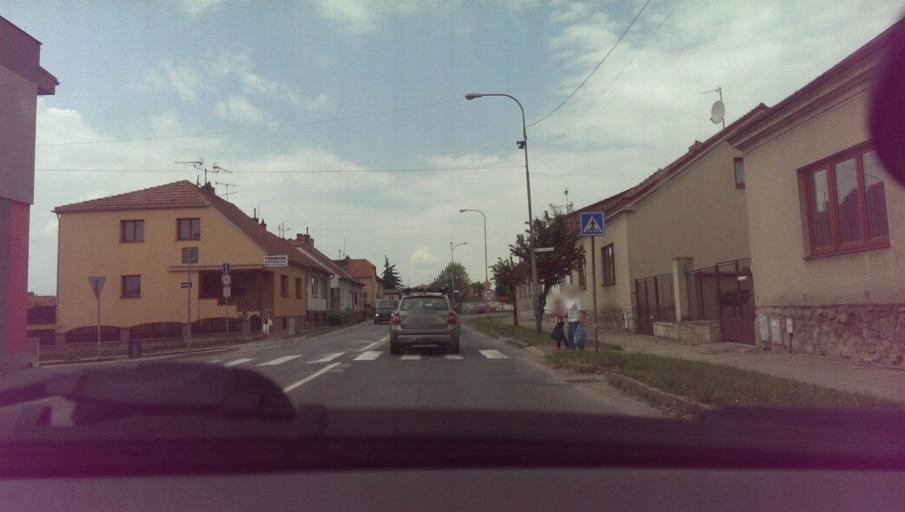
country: CZ
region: South Moravian
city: Slavkov u Brna
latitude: 49.1510
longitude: 16.8750
